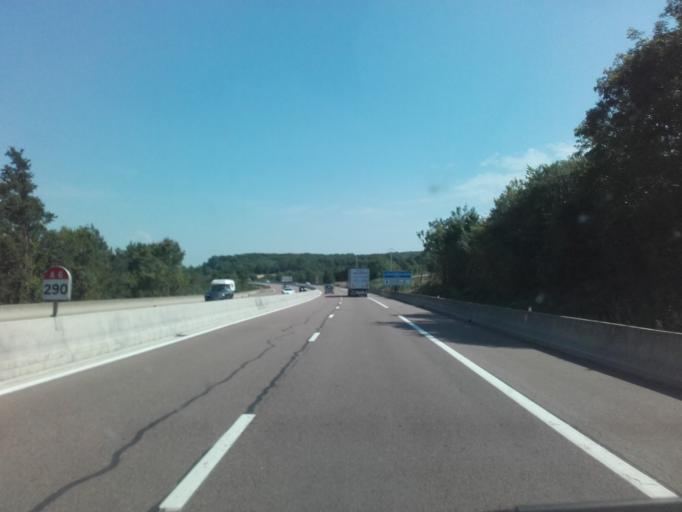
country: FR
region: Bourgogne
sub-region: Departement de la Cote-d'Or
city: Savigny-les-Beaune
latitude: 47.0922
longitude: 4.7510
